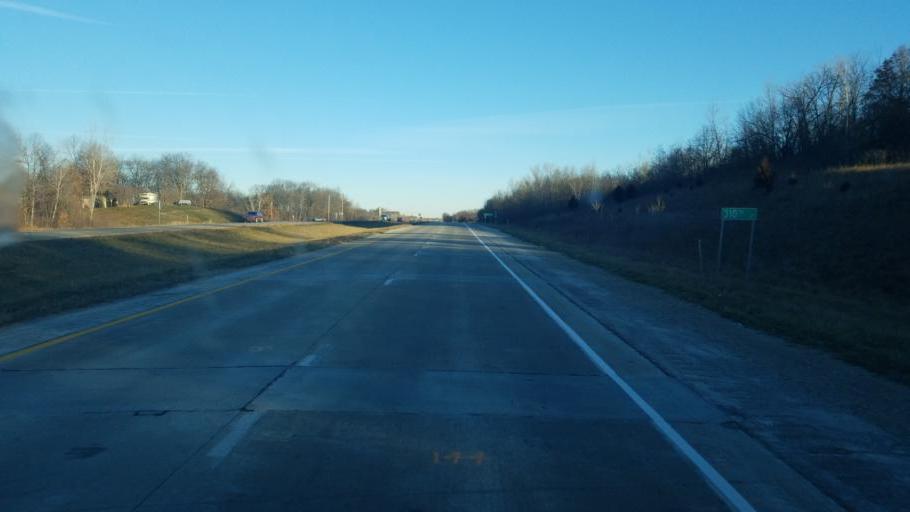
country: US
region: Iowa
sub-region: Wapello County
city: Eddyville
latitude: 41.2023
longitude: -92.6399
